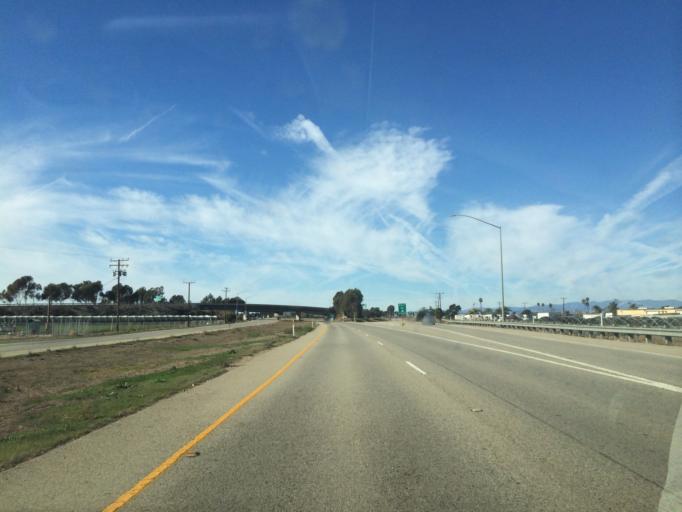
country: US
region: California
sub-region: Ventura County
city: Oxnard
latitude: 34.1597
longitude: -119.1337
